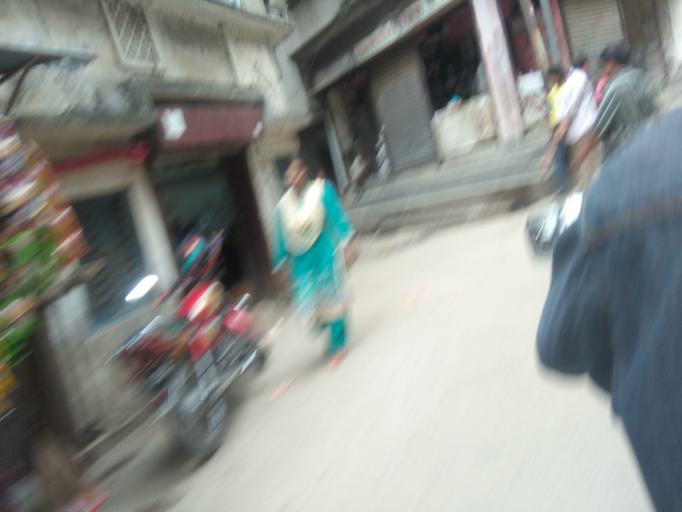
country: BD
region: Dhaka
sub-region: Dhaka
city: Dhaka
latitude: 23.7045
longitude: 90.4154
